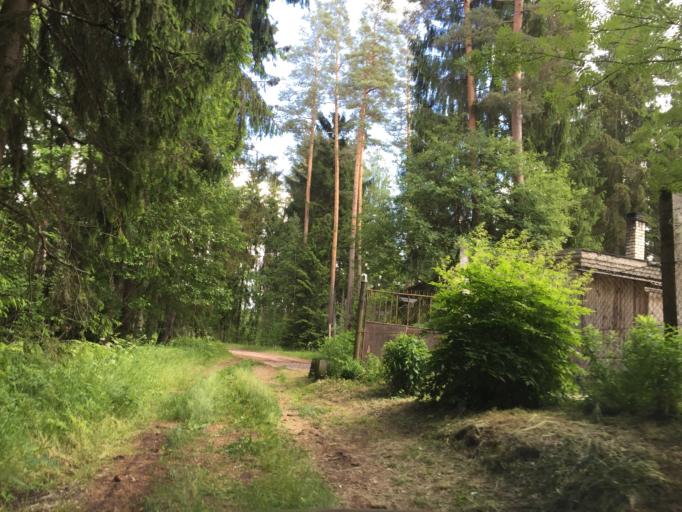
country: LV
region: Lecava
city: Iecava
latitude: 56.5488
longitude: 24.3453
